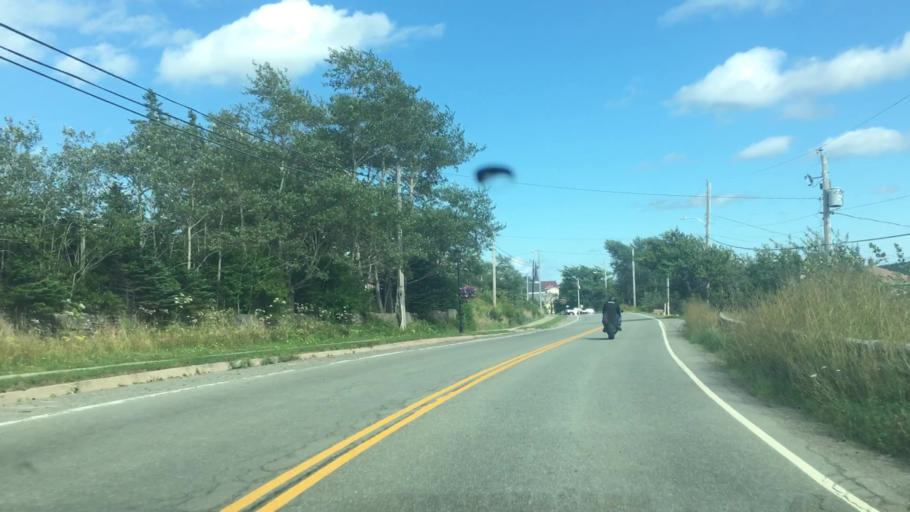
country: CA
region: Nova Scotia
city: Princeville
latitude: 45.6556
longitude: -60.8863
